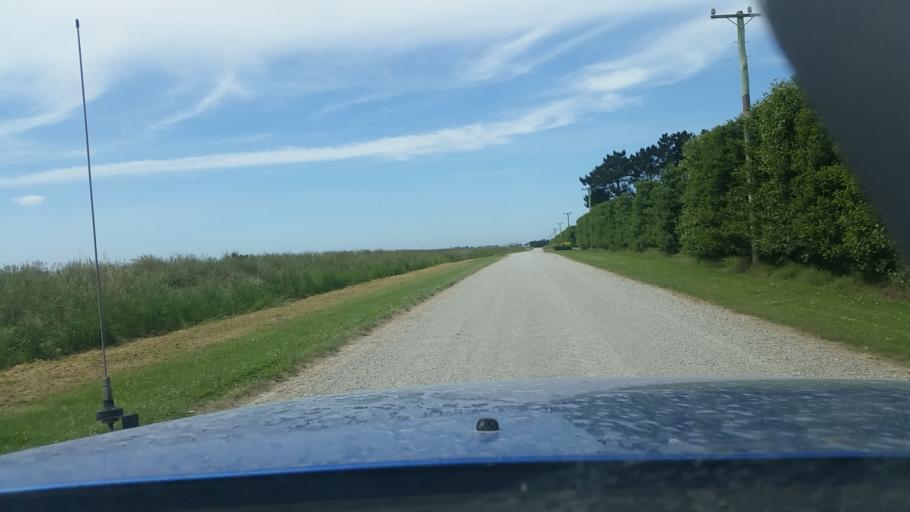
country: NZ
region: Canterbury
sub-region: Ashburton District
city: Tinwald
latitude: -44.0756
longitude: 171.7195
